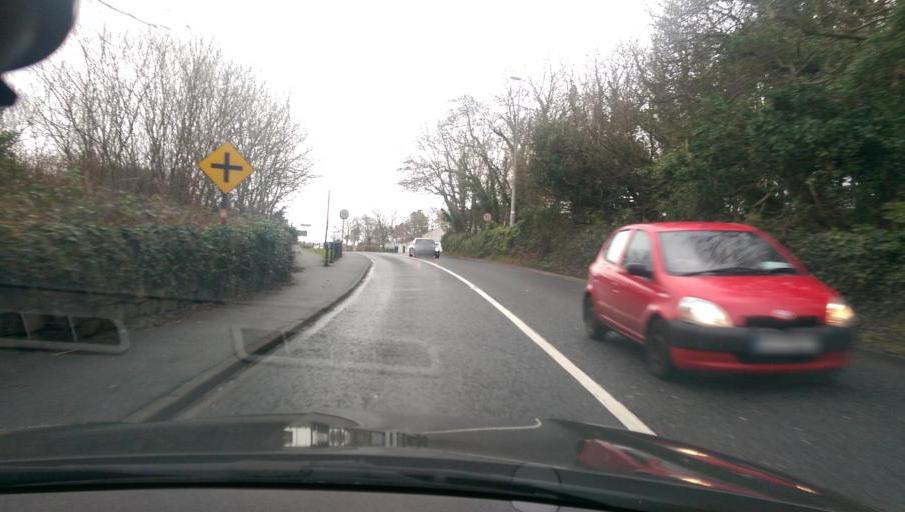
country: IE
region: Connaught
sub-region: County Galway
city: Bearna
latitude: 53.2577
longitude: -9.1326
